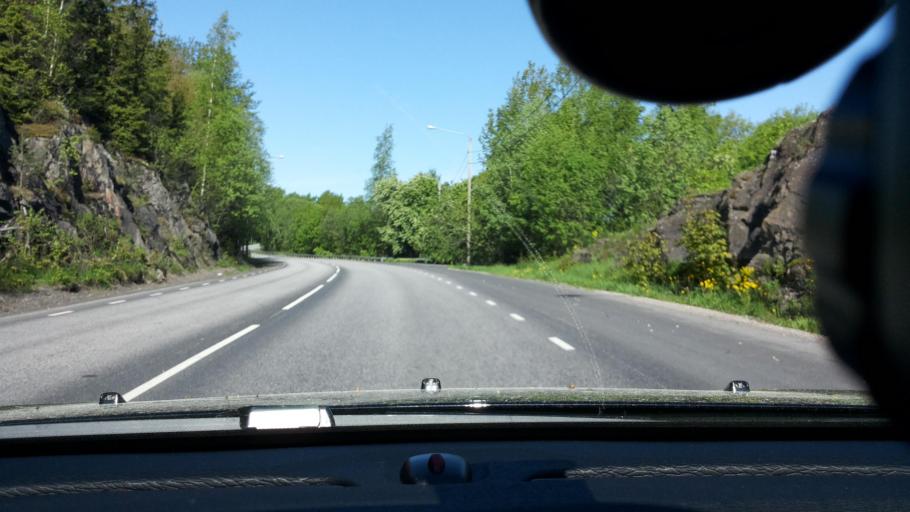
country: SE
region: Vaesternorrland
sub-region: Sundsvalls Kommun
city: Sundsbruk
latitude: 62.4657
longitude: 17.3371
